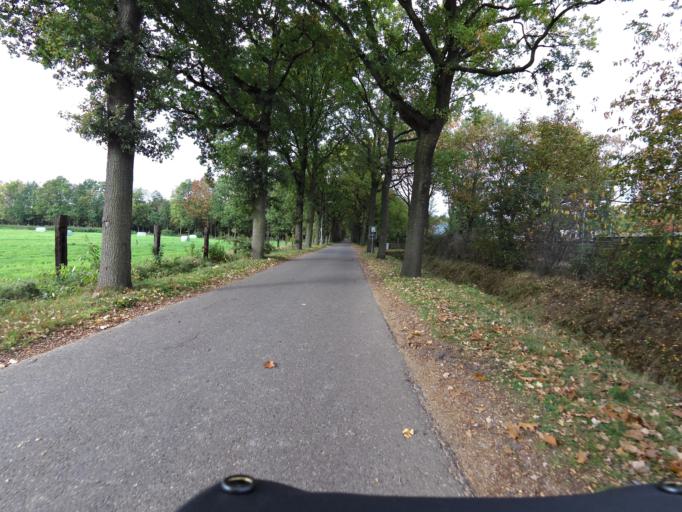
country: BE
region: Flanders
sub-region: Provincie Antwerpen
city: Stabroek
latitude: 51.3699
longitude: 4.3986
